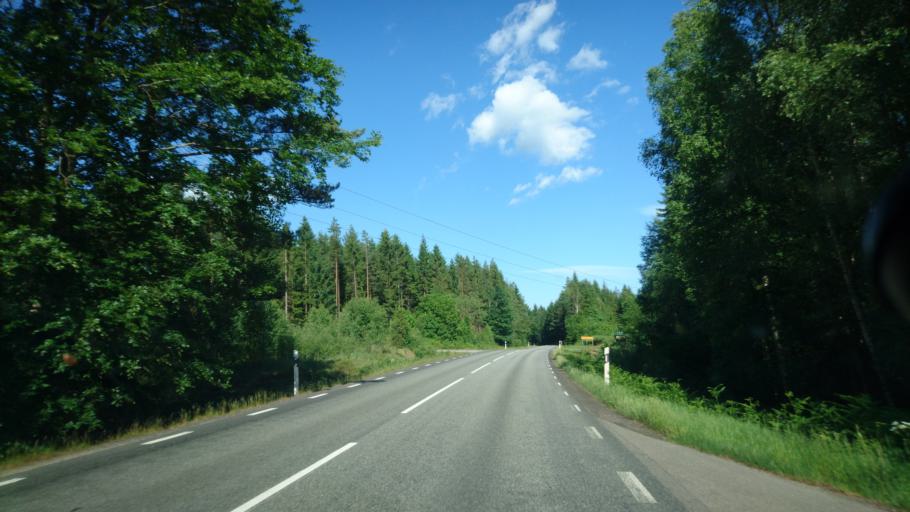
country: SE
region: Skane
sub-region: Osby Kommun
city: Lonsboda
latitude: 56.3893
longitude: 14.4112
